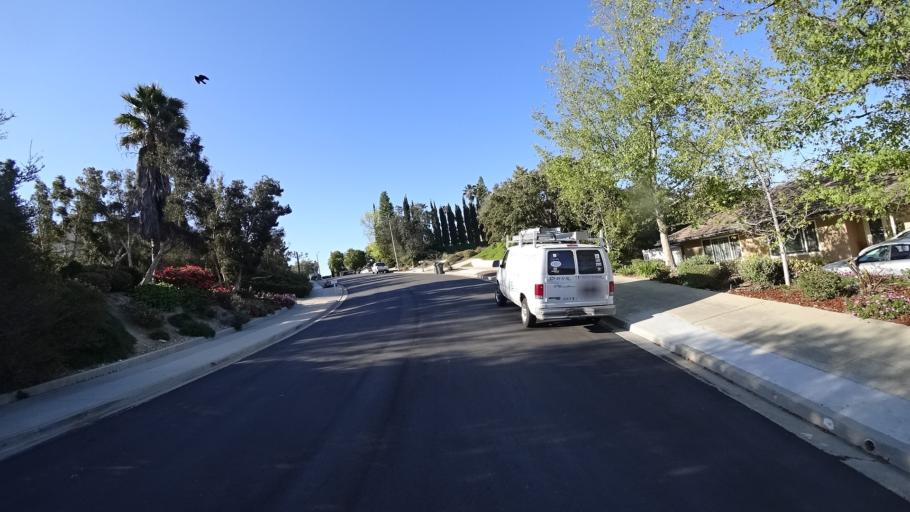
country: US
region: California
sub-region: Ventura County
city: Thousand Oaks
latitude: 34.1929
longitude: -118.8386
